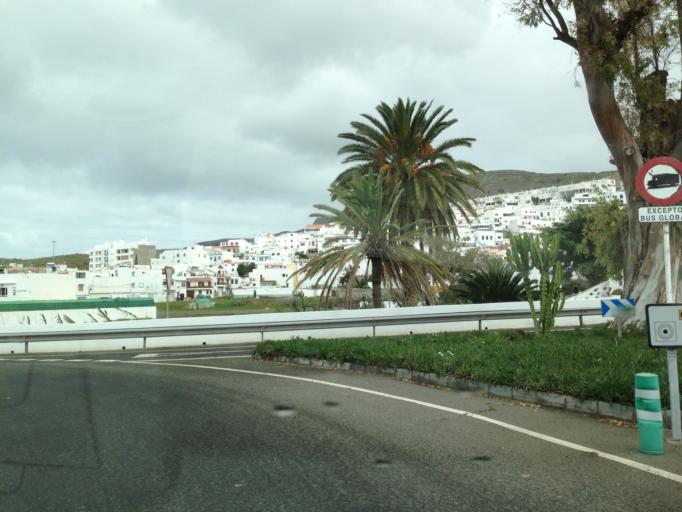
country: ES
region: Canary Islands
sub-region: Provincia de Las Palmas
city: Agaete
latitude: 28.0995
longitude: -15.7034
